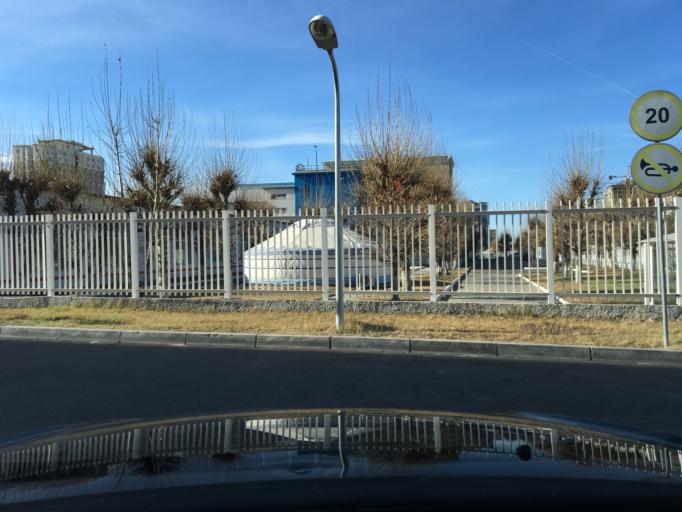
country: MN
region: Ulaanbaatar
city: Ulaanbaatar
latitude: 47.8989
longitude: 106.9055
